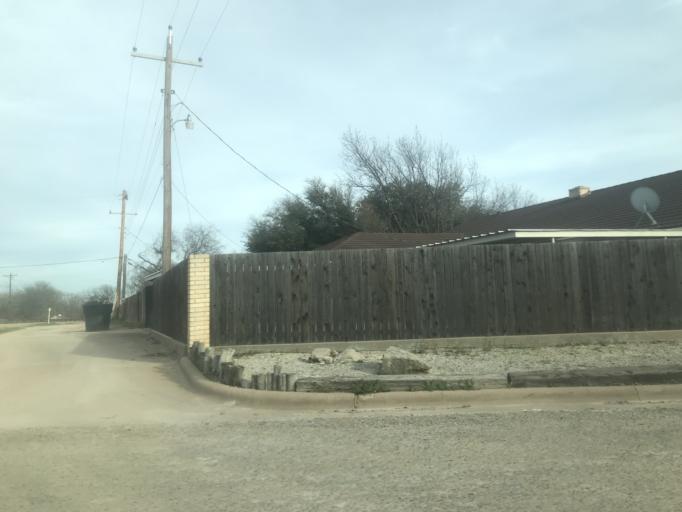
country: US
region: Texas
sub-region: Taylor County
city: Abilene
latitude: 32.3947
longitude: -99.7572
